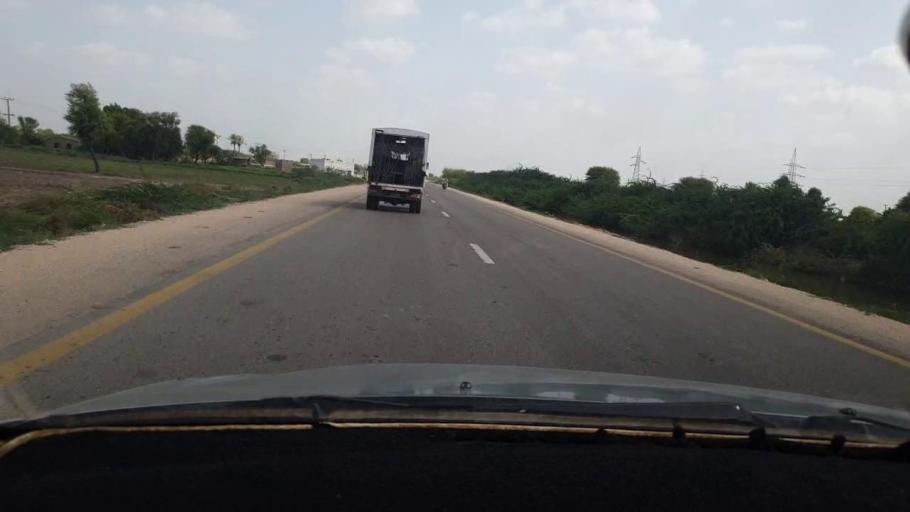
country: PK
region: Sindh
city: Digri
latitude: 25.0340
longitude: 69.2419
